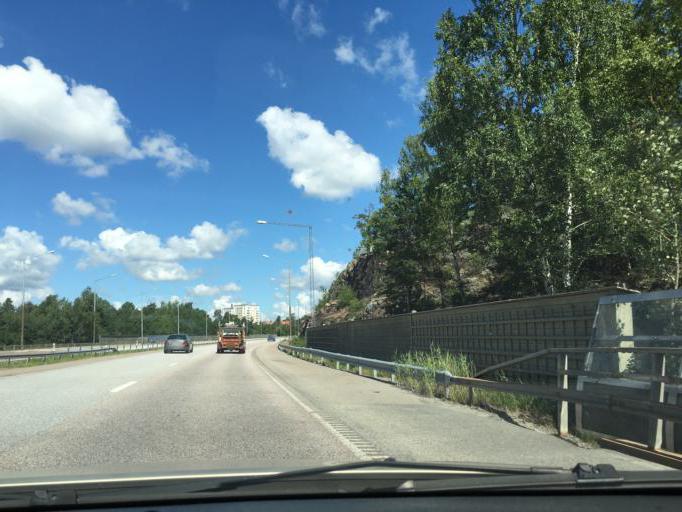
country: SE
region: Stockholm
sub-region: Nacka Kommun
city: Nacka
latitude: 59.3044
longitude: 18.1827
